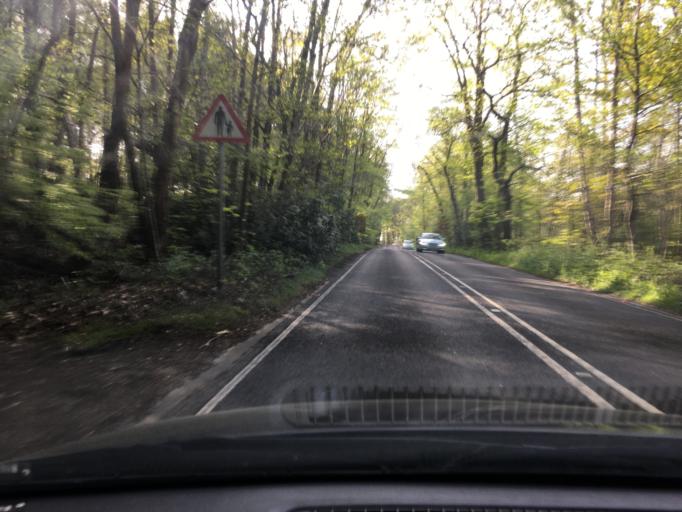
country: GB
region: England
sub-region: Bracknell Forest
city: Bracknell
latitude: 51.3875
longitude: -0.7587
